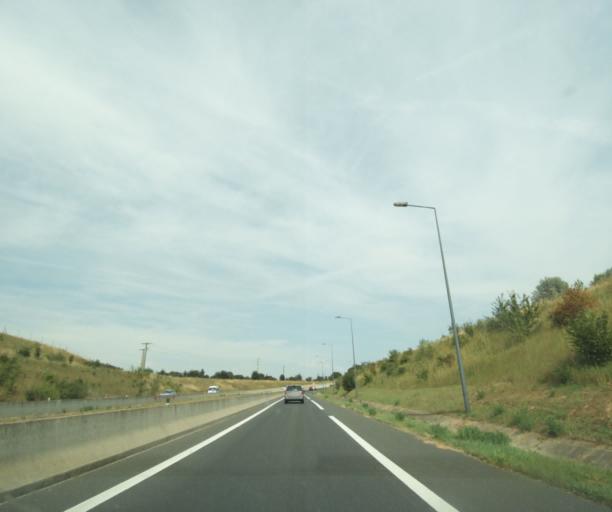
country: FR
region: Centre
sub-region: Departement d'Indre-et-Loire
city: La Membrolle-sur-Choisille
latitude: 47.4311
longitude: 0.6508
